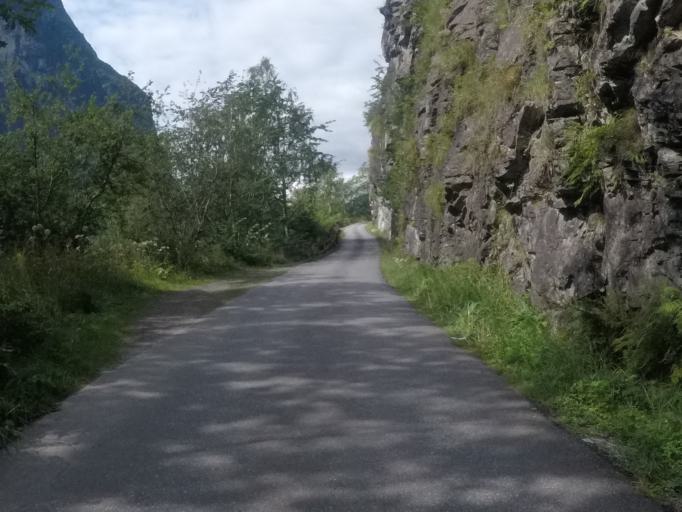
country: NO
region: Sogn og Fjordane
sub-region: Stryn
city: Stryn
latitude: 61.7874
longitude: 6.9994
